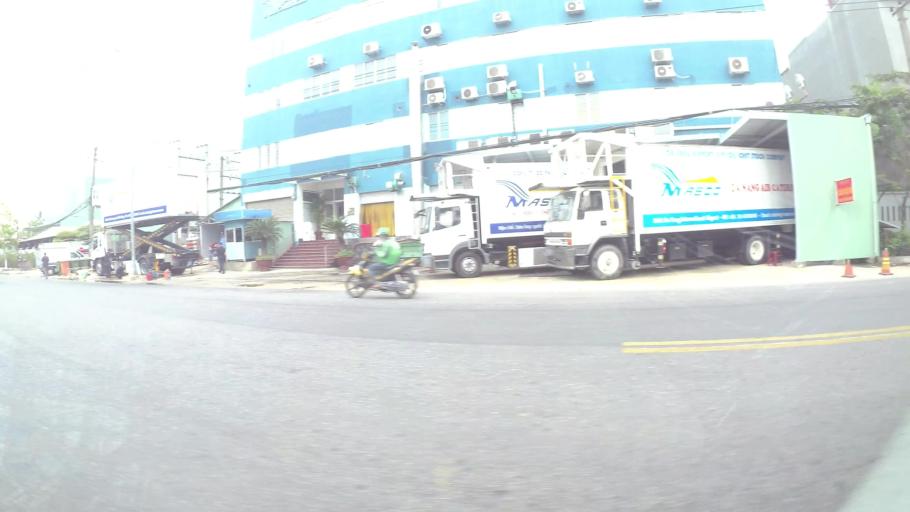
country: VN
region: Da Nang
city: Thanh Khe
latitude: 16.0544
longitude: 108.2042
